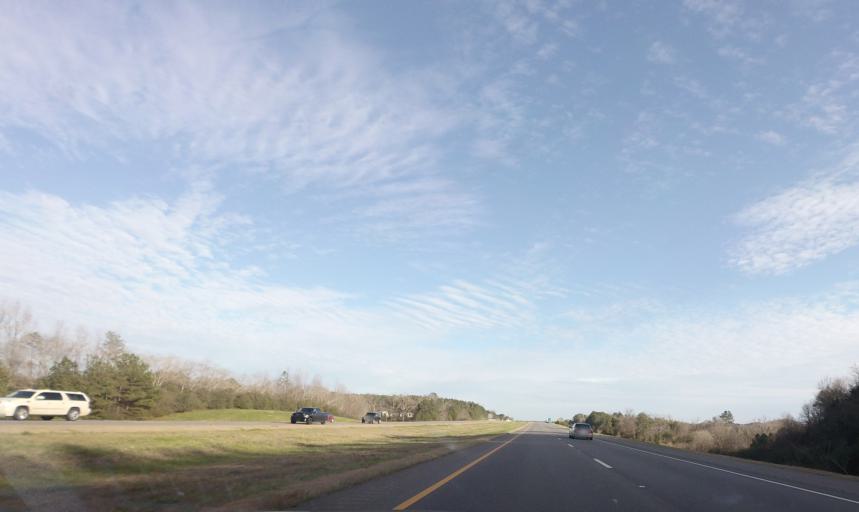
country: US
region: Alabama
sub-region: Walker County
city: Jasper
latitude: 33.8120
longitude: -87.3026
